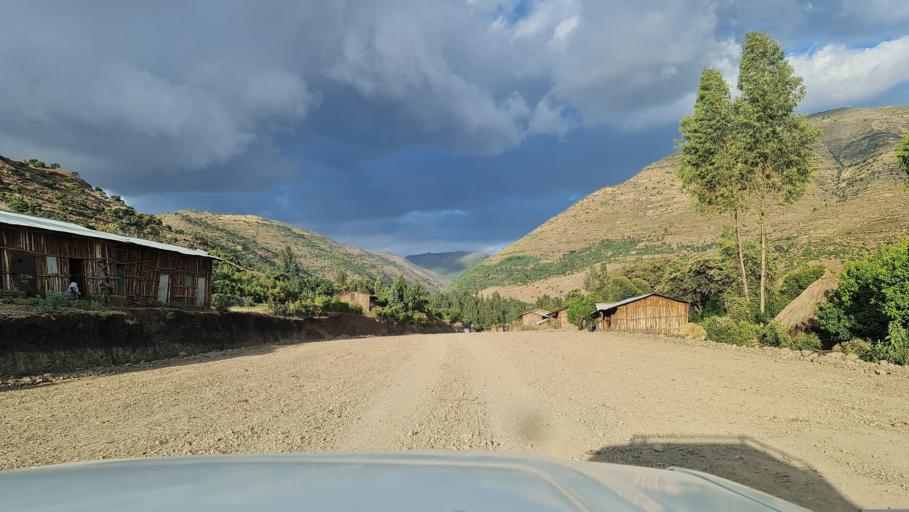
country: ET
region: Amhara
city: Debark'
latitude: 13.0396
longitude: 38.0512
